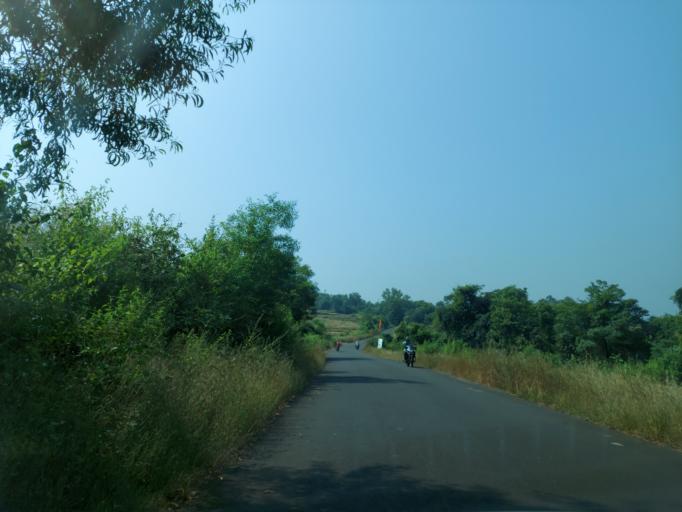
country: IN
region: Maharashtra
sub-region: Sindhudurg
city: Kudal
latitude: 15.9759
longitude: 73.6509
